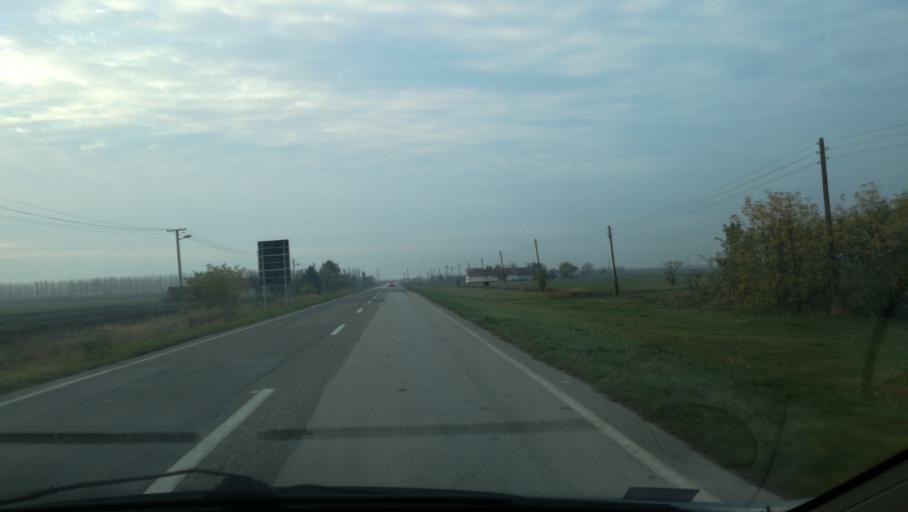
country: RS
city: Basaid
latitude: 45.6811
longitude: 20.4231
